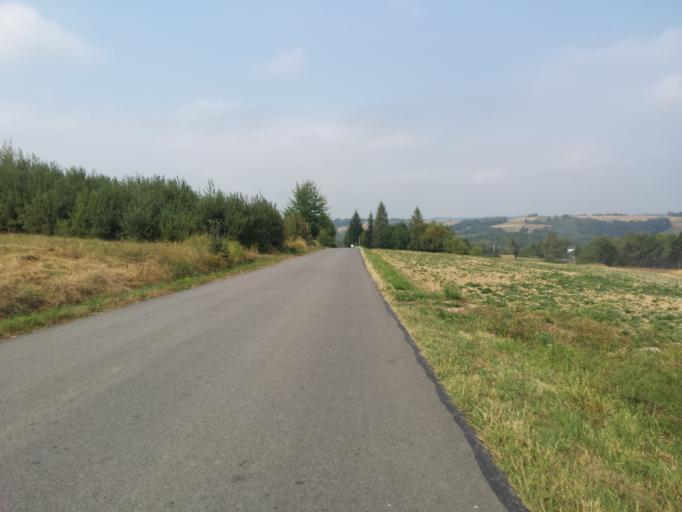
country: PL
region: Subcarpathian Voivodeship
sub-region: Powiat rzeszowski
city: Dynow
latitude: 49.8254
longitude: 22.2054
